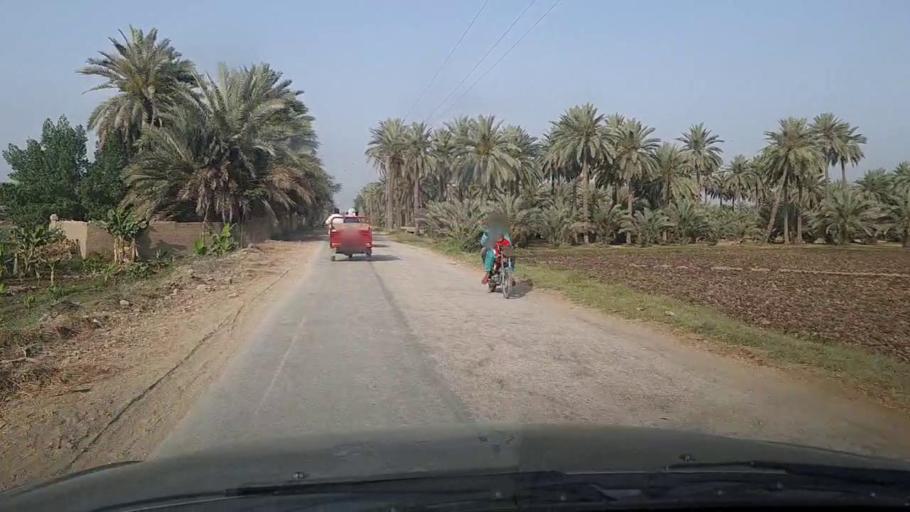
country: PK
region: Sindh
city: Pir jo Goth
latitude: 27.5658
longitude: 68.5770
